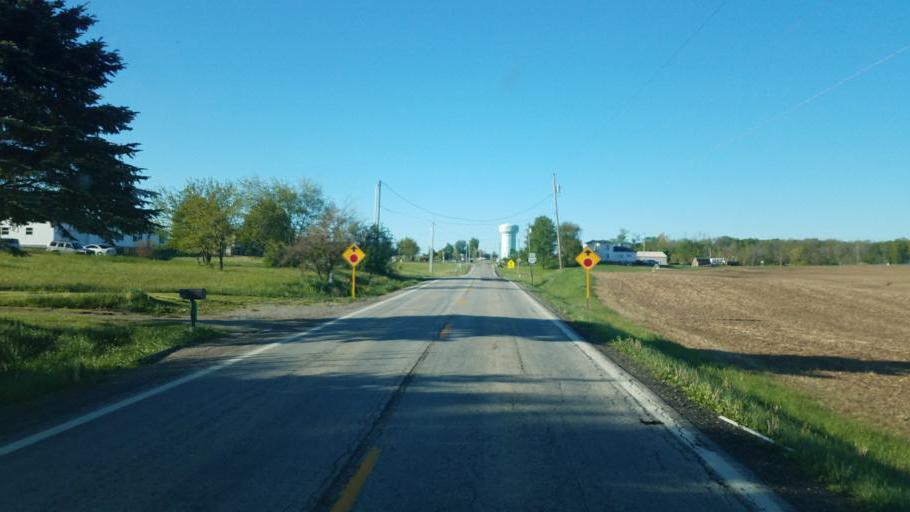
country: US
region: Ohio
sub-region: Knox County
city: Centerburg
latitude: 40.4012
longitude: -82.7071
